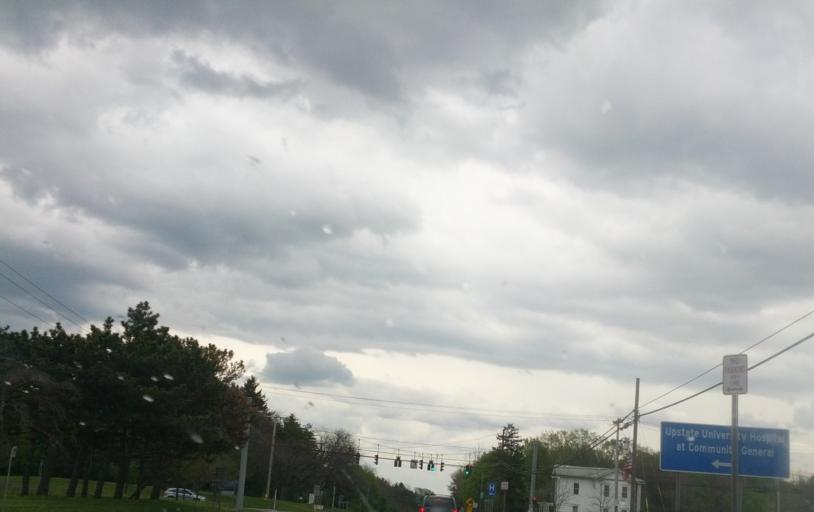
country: US
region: New York
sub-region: Onondaga County
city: Nedrow
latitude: 43.0053
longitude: -76.1714
